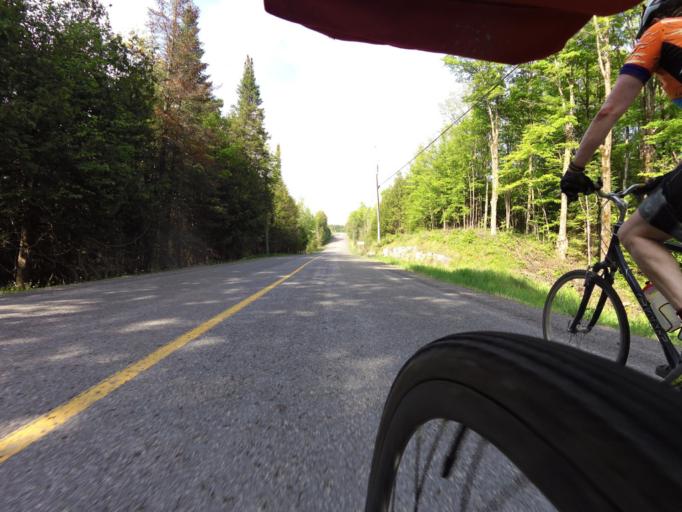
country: CA
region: Ontario
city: Arnprior
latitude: 45.1707
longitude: -76.4746
